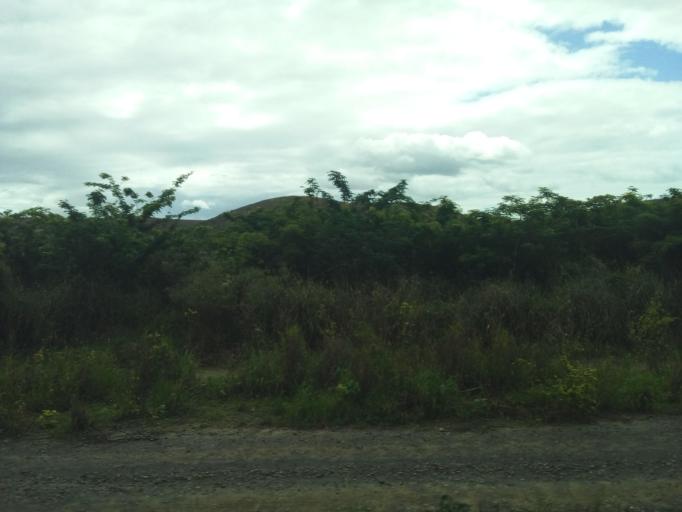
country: BR
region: Minas Gerais
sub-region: Governador Valadares
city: Governador Valadares
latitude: -19.0853
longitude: -42.1619
